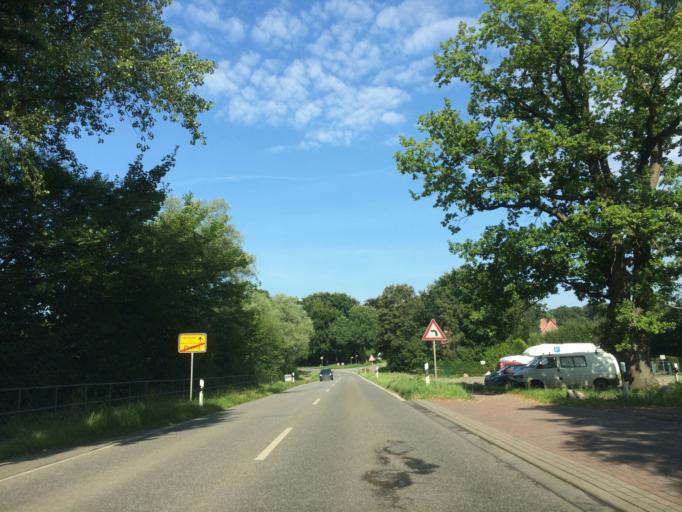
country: DE
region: Schleswig-Holstein
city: Preetz
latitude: 54.2444
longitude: 10.2699
